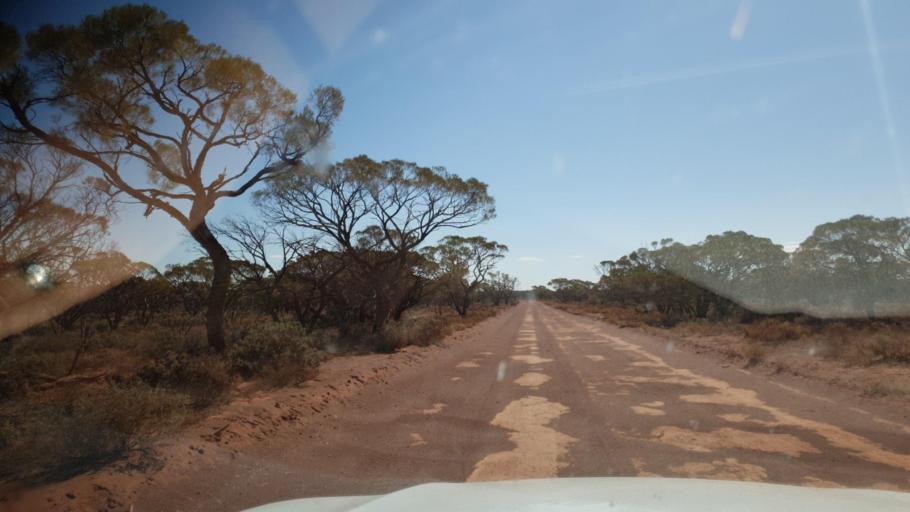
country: AU
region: South Australia
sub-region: Kimba
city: Caralue
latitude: -32.5229
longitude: 136.1445
